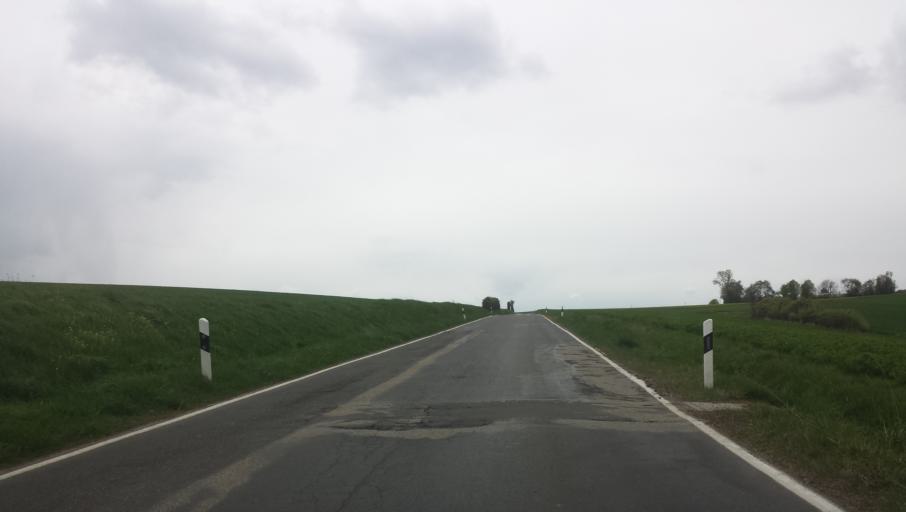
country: DE
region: Rheinland-Pfalz
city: Morsfeld
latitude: 49.7407
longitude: 7.9272
